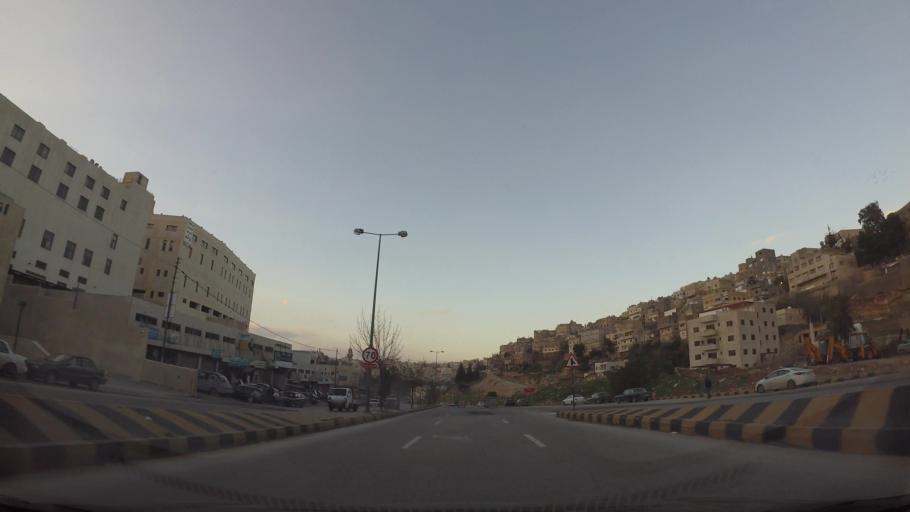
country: JO
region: Amman
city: Al Bunayyat ash Shamaliyah
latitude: 31.9210
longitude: 35.9118
